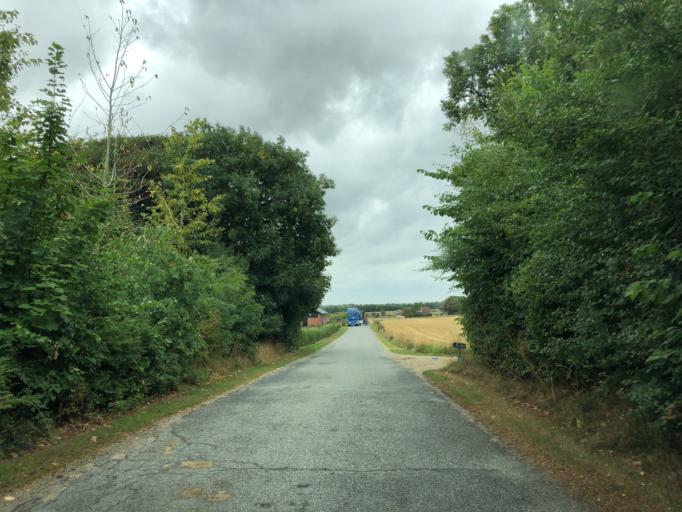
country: DK
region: Central Jutland
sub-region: Ringkobing-Skjern Kommune
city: Videbaek
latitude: 56.1023
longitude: 8.4885
